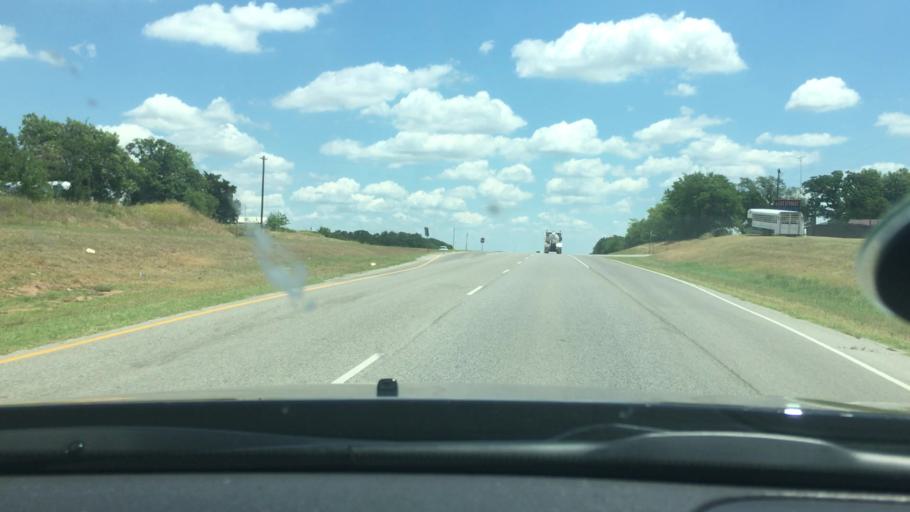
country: US
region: Oklahoma
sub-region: Carter County
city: Wilson
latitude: 34.1728
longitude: -97.3884
